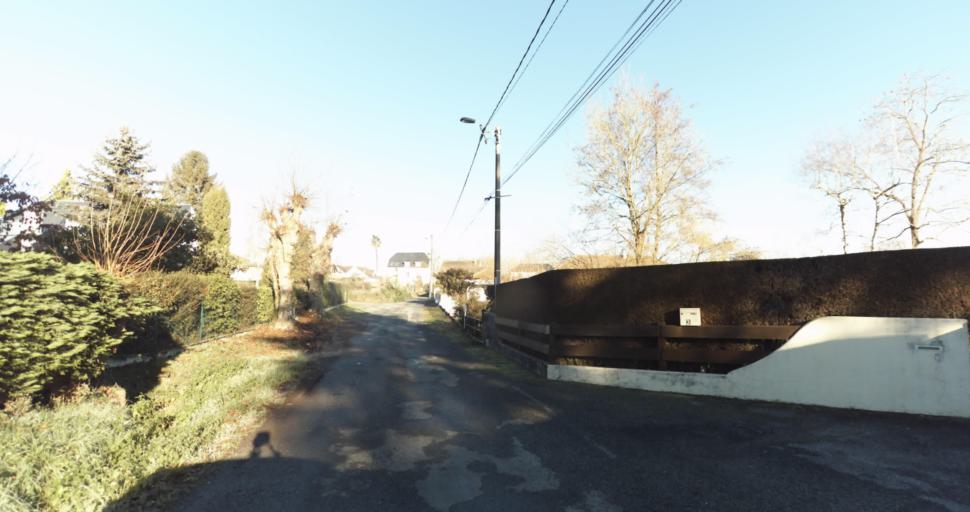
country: FR
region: Aquitaine
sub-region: Departement des Pyrenees-Atlantiques
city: Morlaas
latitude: 43.3397
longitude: -0.2631
